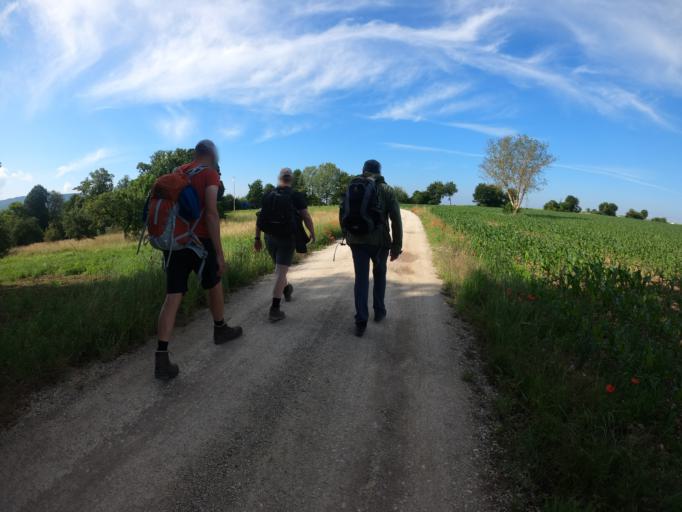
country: DE
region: Bavaria
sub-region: Upper Franconia
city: Litzendorf
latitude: 49.8783
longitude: 11.0103
